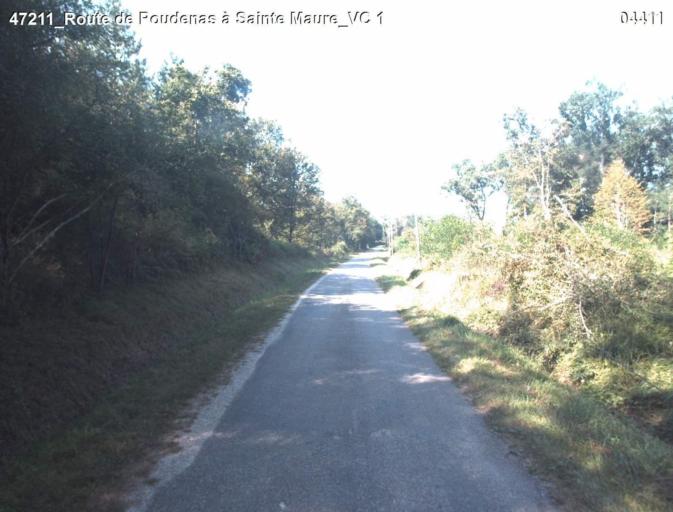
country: FR
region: Midi-Pyrenees
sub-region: Departement du Gers
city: Montreal
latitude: 44.0155
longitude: 0.1903
